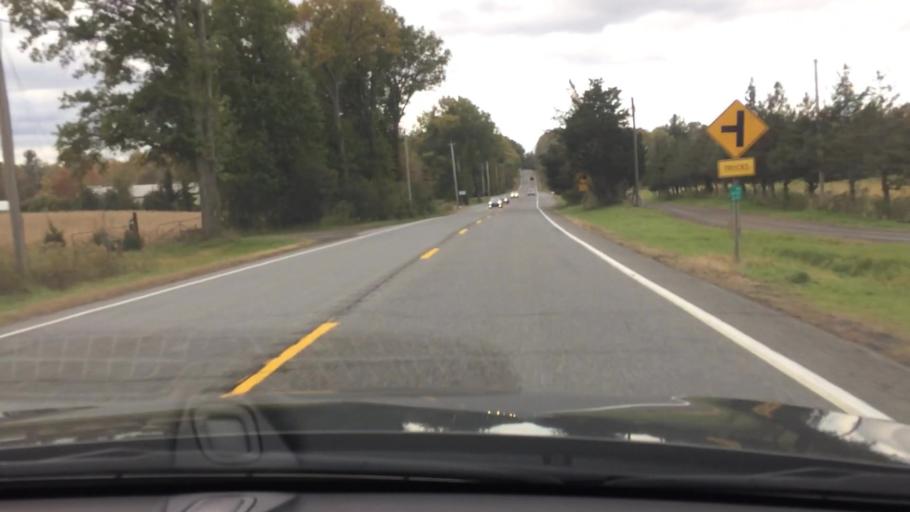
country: US
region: New York
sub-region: Columbia County
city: Kinderhook
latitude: 42.3755
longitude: -73.6941
